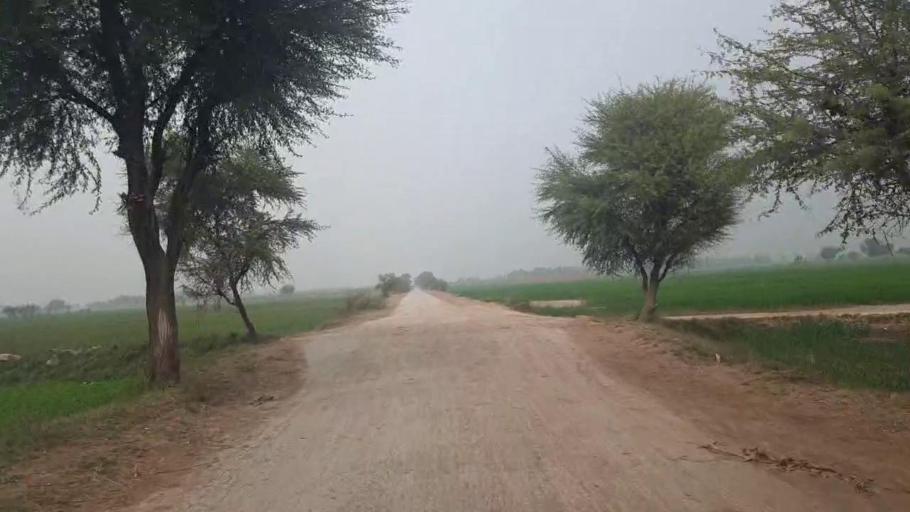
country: PK
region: Sindh
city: Tando Adam
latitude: 25.7589
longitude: 68.7026
